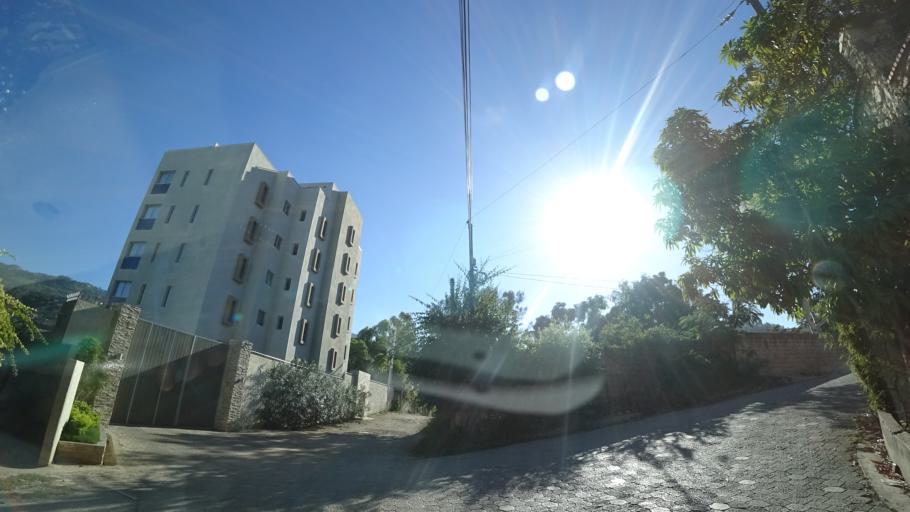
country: HT
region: Ouest
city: Petionville
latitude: 18.5068
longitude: -72.2962
